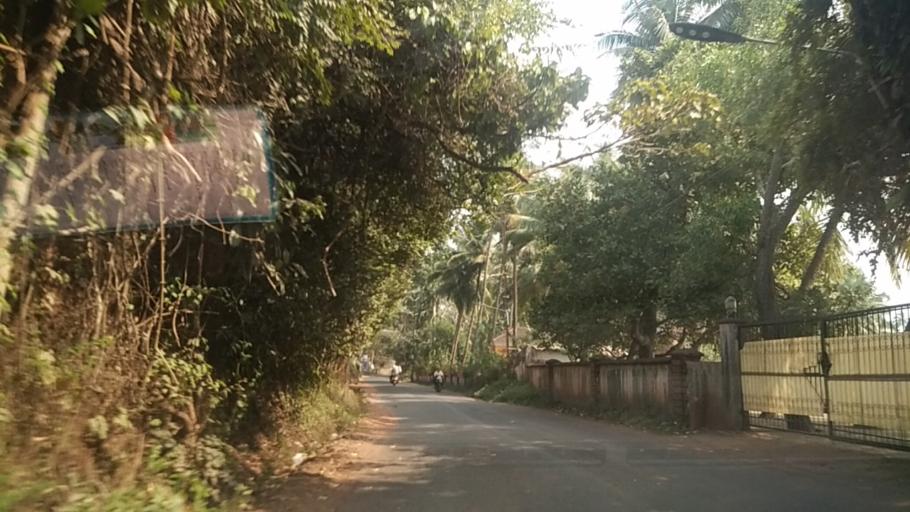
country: IN
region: Goa
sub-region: North Goa
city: Panaji
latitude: 15.5092
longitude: 73.8225
